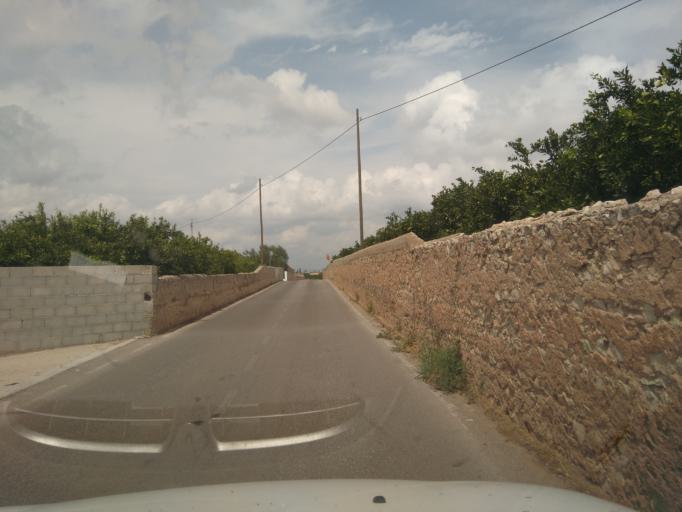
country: ES
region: Valencia
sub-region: Provincia de Valencia
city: Carcaixent
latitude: 39.1091
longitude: -0.4356
